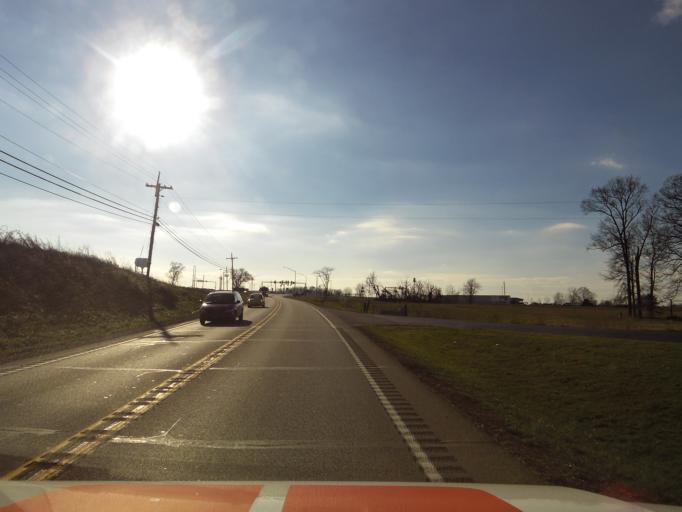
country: US
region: Indiana
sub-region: Jackson County
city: Seymour
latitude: 38.9612
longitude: -85.8320
